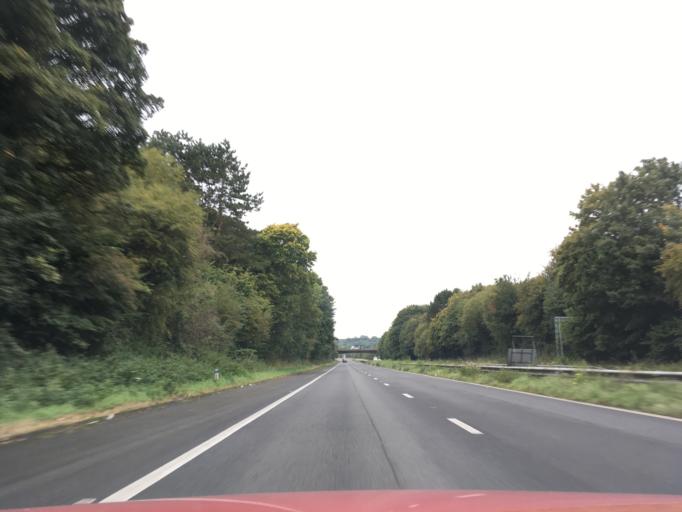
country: GB
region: Wales
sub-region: Monmouthshire
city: Chepstow
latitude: 51.6167
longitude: -2.7033
